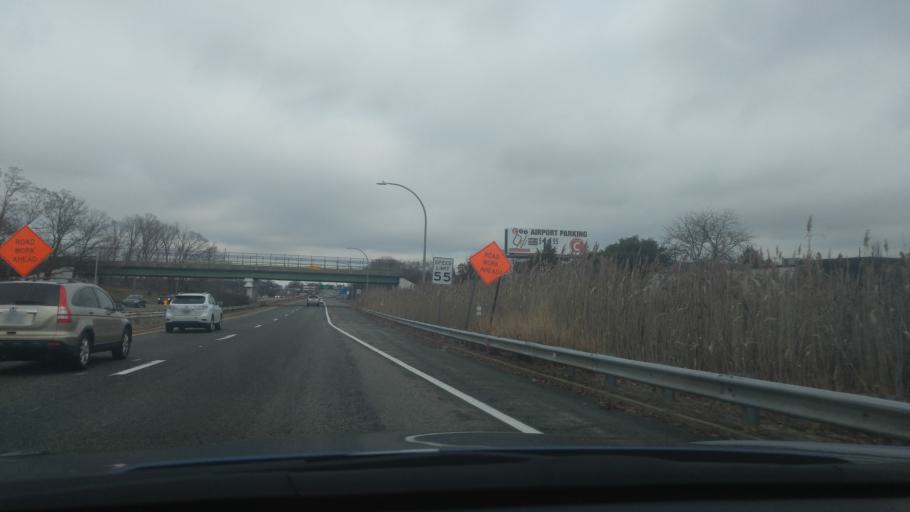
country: US
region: Rhode Island
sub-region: Kent County
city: Warwick
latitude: 41.7272
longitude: -71.4562
